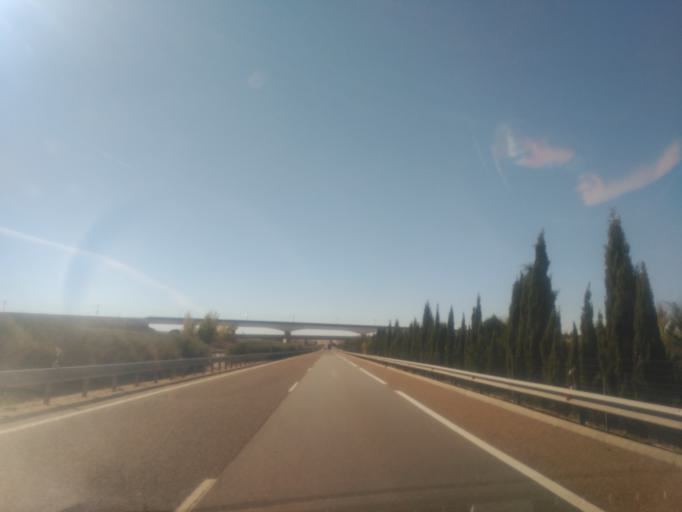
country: ES
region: Castille and Leon
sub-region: Provincia de Valladolid
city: Siete Iglesias de Trabancos
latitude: 41.3810
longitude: -5.1532
